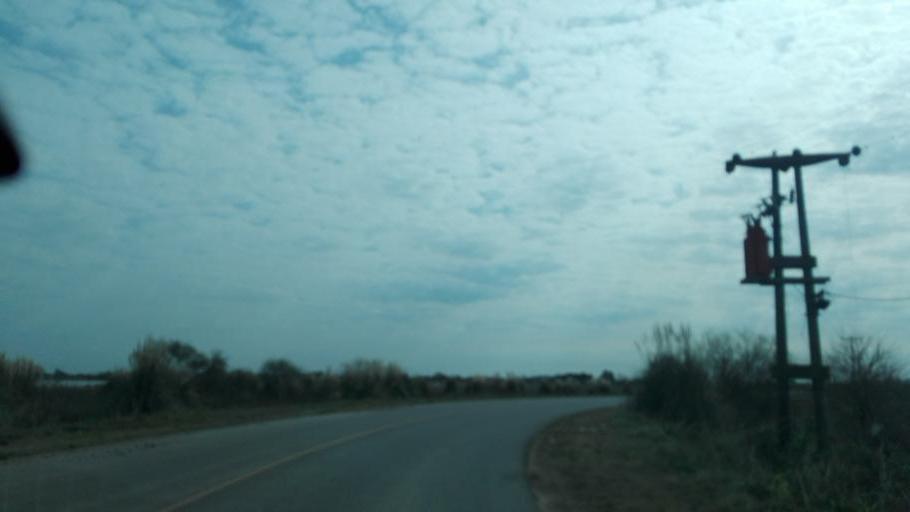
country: AR
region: Buenos Aires
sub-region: Partido de Chascomus
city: Chascomus
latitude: -35.5594
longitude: -58.0388
